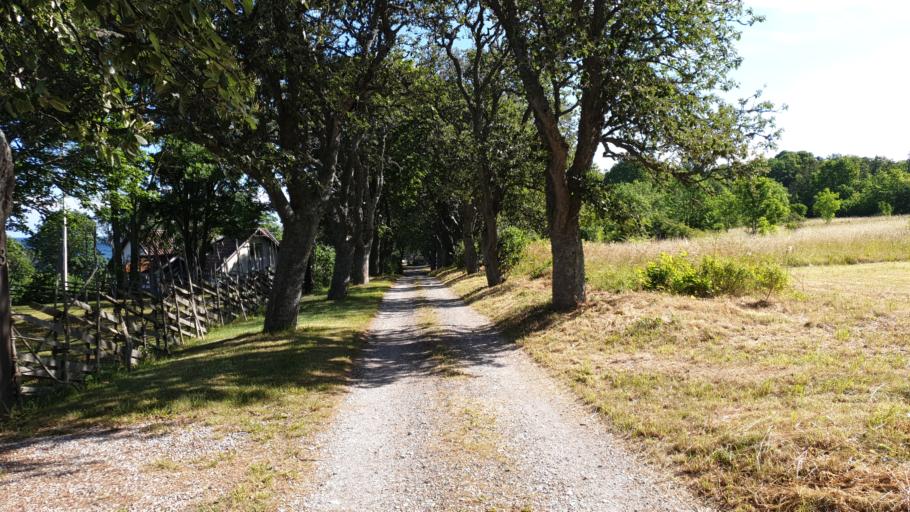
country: SE
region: Gotland
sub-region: Gotland
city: Vibble
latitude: 57.5985
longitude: 18.2127
